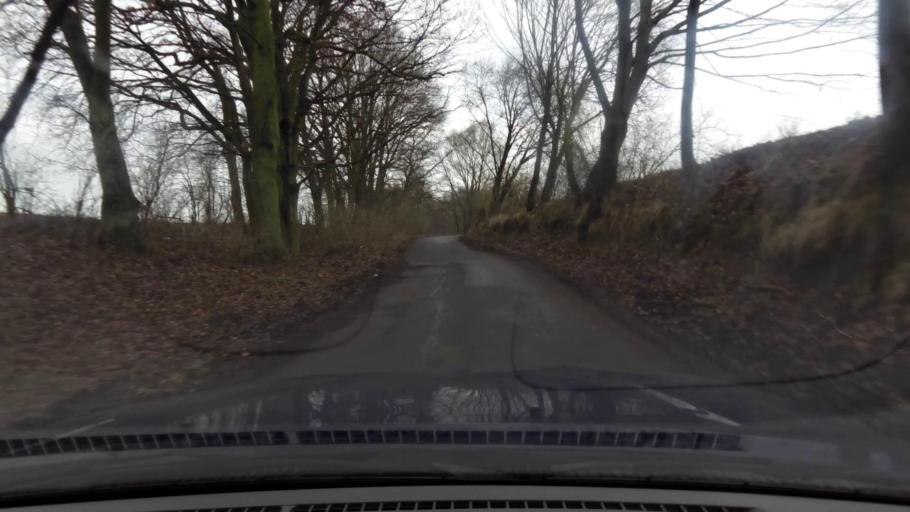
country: PL
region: West Pomeranian Voivodeship
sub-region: Powiat stargardzki
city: Stargard Szczecinski
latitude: 53.3322
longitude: 15.1303
